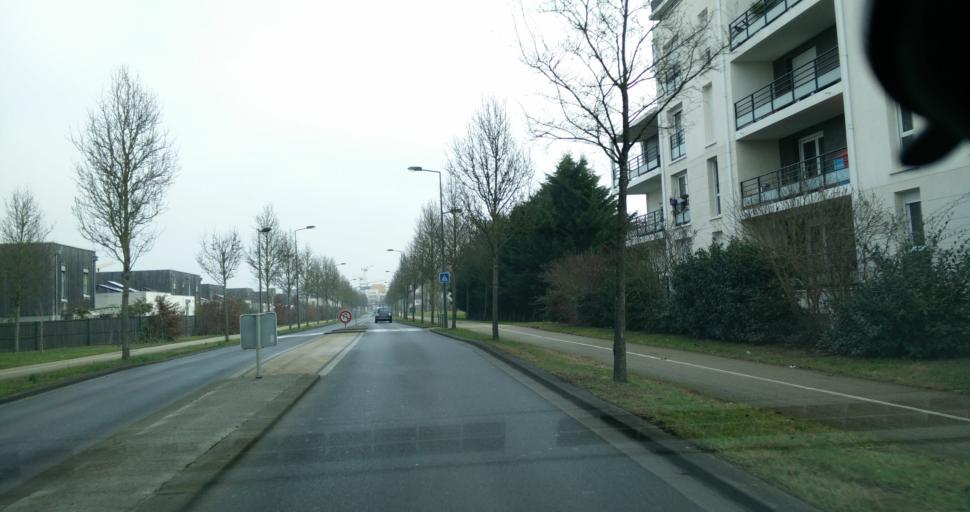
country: FR
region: Centre
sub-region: Departement d'Indre-et-Loire
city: Saint-Cyr-sur-Loire
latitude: 47.4186
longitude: 0.6864
